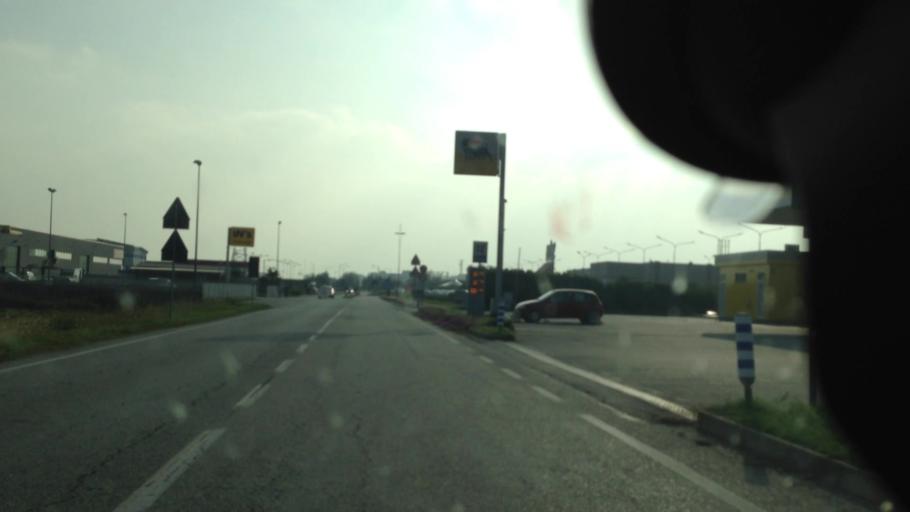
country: IT
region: Piedmont
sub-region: Provincia di Vercelli
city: Cigliano
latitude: 45.3206
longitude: 8.0318
